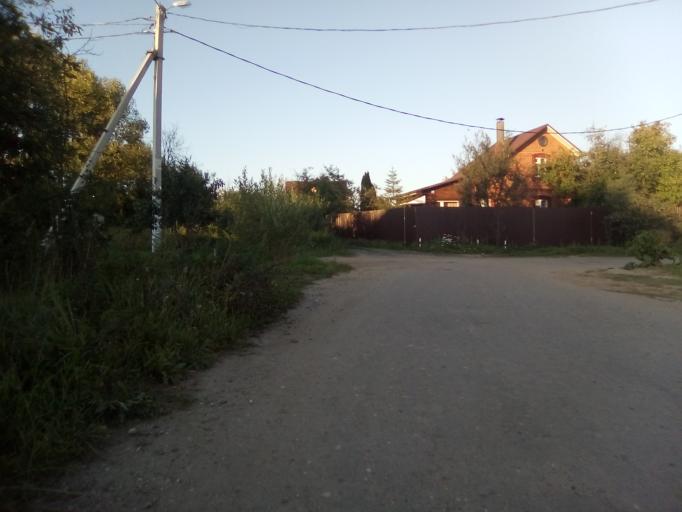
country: RU
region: Moskovskaya
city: Krasnoznamensk
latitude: 55.5732
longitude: 37.0328
